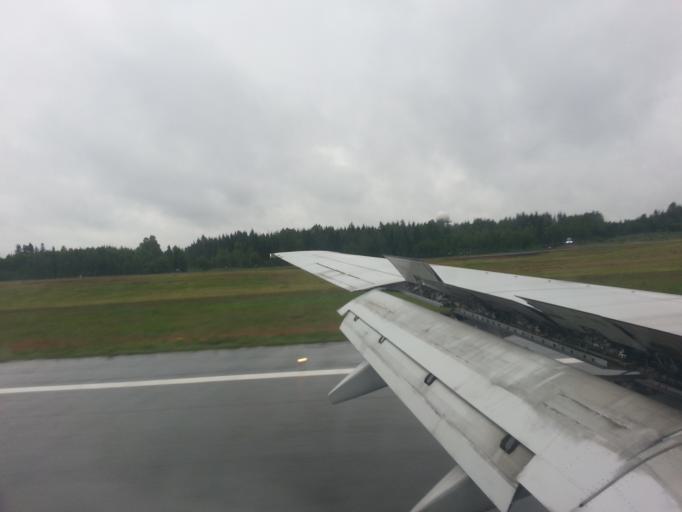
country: NO
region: Akershus
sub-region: Ullensaker
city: Jessheim
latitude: 60.1927
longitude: 11.1170
